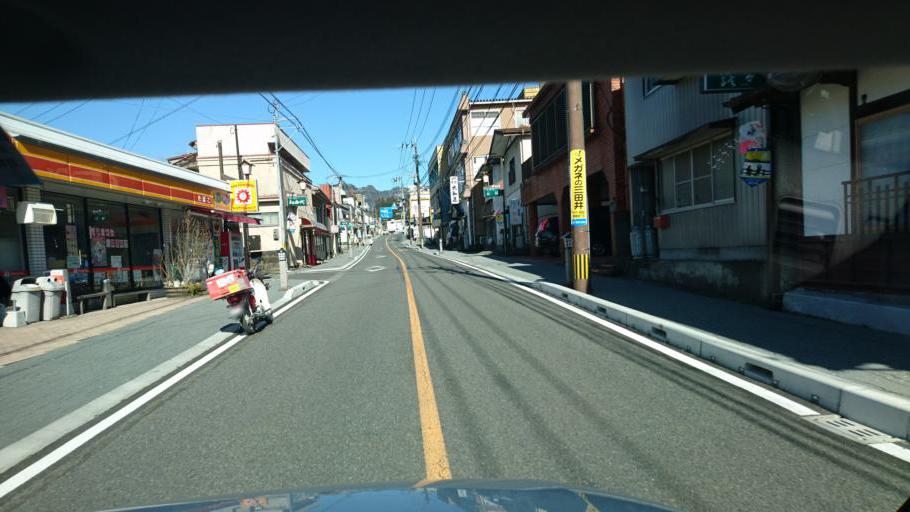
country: JP
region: Oita
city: Takedamachi
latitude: 32.7089
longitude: 131.3064
